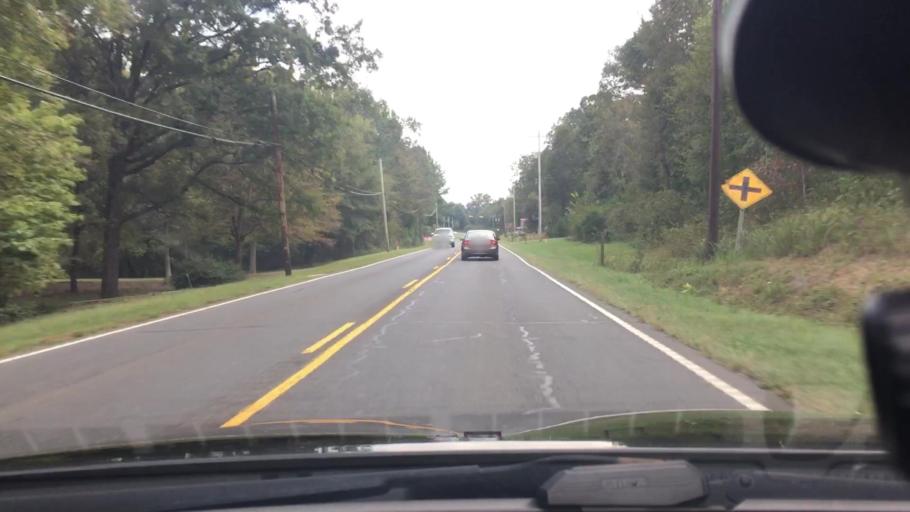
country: US
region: North Carolina
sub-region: Stanly County
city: Albemarle
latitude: 35.3326
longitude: -80.1346
